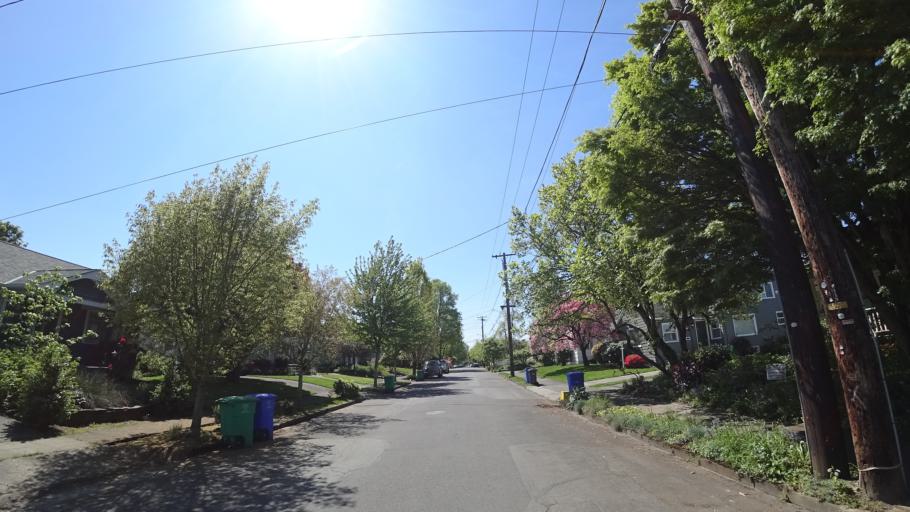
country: US
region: Oregon
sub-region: Clackamas County
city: Milwaukie
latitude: 45.4785
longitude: -122.6434
